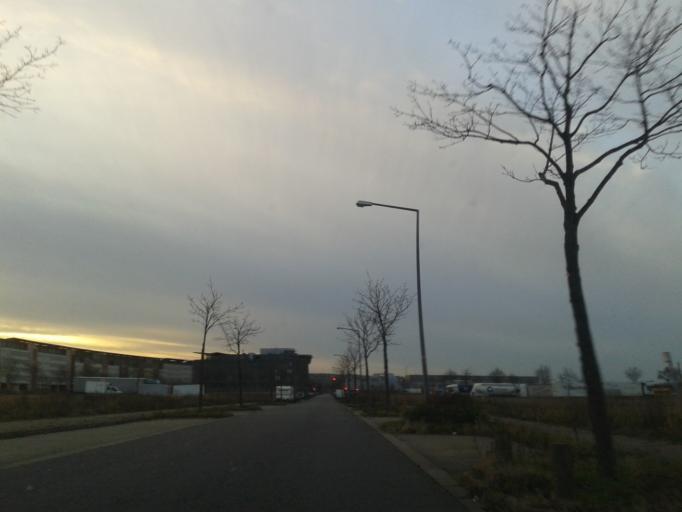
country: DE
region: Saxony
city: Dresden
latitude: 51.0783
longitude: 13.7017
